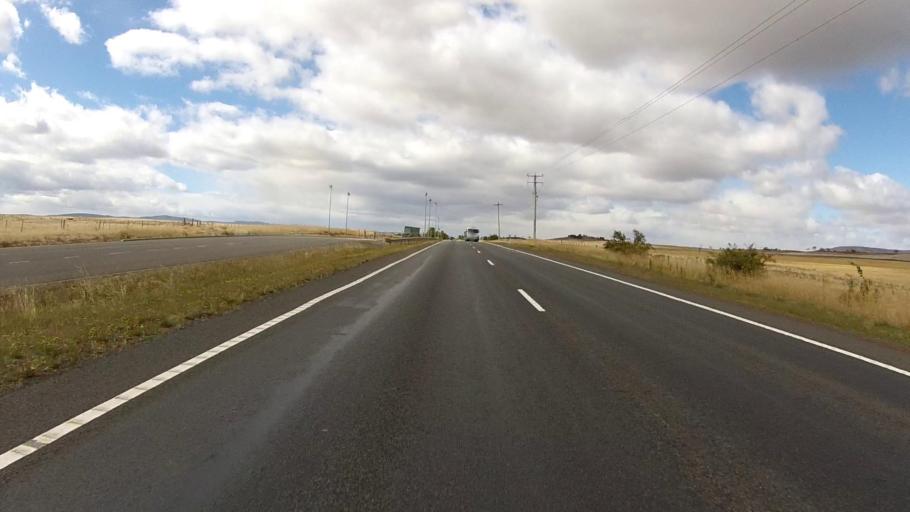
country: AU
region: Tasmania
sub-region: Northern Midlands
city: Evandale
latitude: -41.8832
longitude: 147.4663
